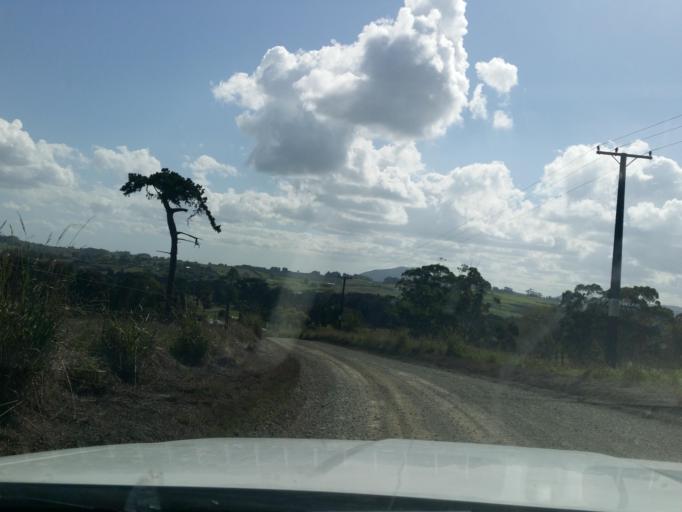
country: NZ
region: Auckland
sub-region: Auckland
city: Wellsford
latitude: -36.1502
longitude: 174.5169
